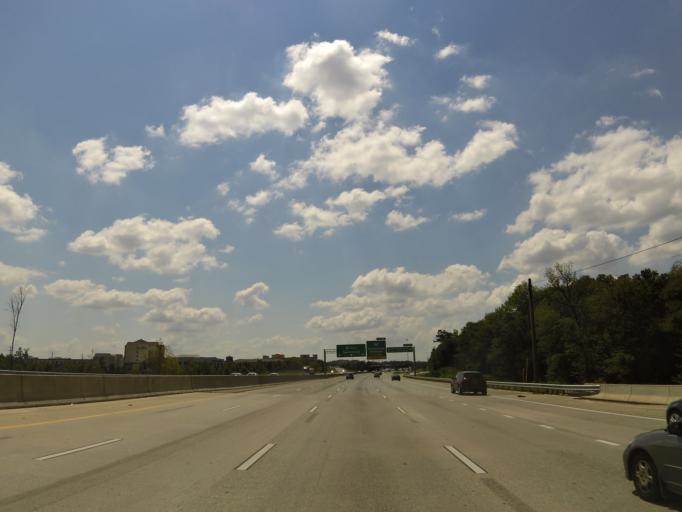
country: US
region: North Carolina
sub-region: Cabarrus County
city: Harrisburg
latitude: 35.3742
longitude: -80.7095
